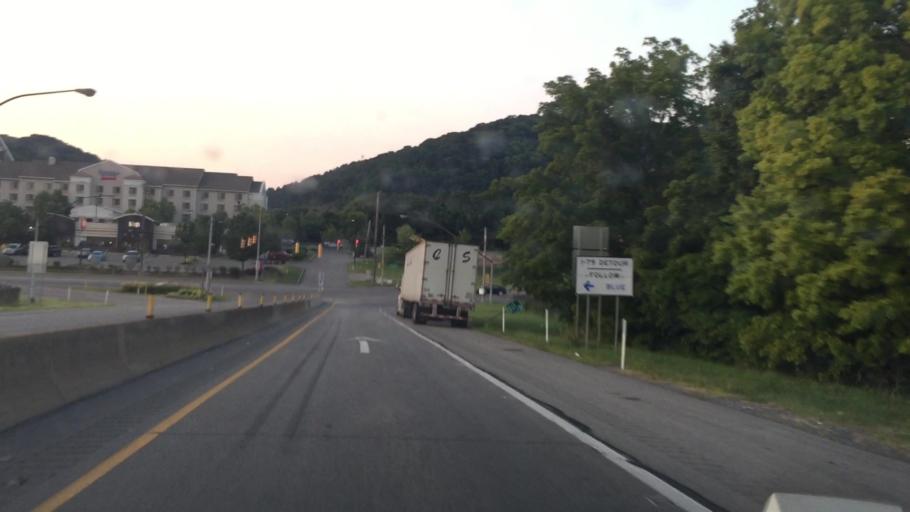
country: US
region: Pennsylvania
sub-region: Allegheny County
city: Coraopolis
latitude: 40.5115
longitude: -80.1335
